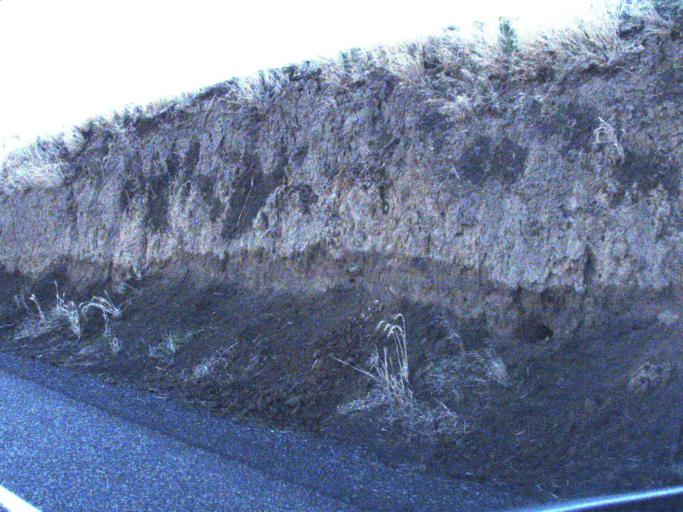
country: US
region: Washington
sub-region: Garfield County
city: Pomeroy
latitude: 46.7349
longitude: -117.7544
